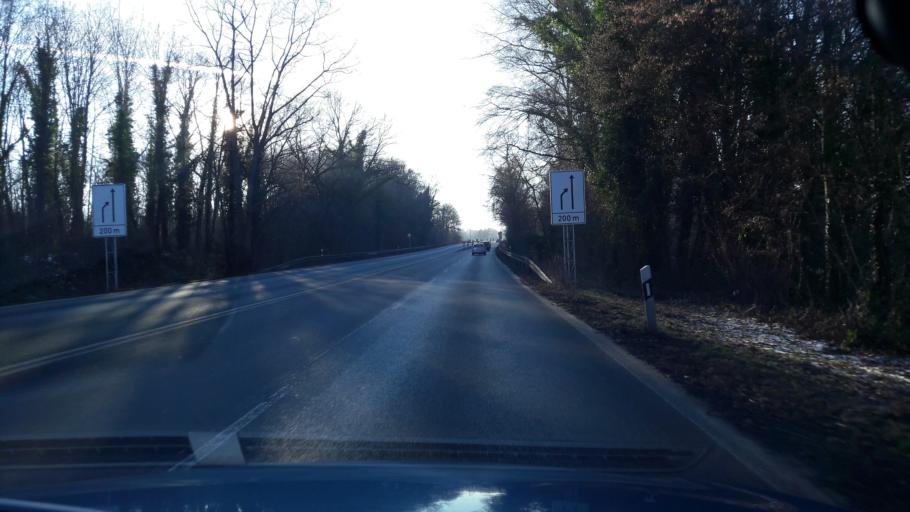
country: DE
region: North Rhine-Westphalia
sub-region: Regierungsbezirk Arnsberg
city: Lippstadt
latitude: 51.7060
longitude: 8.3592
